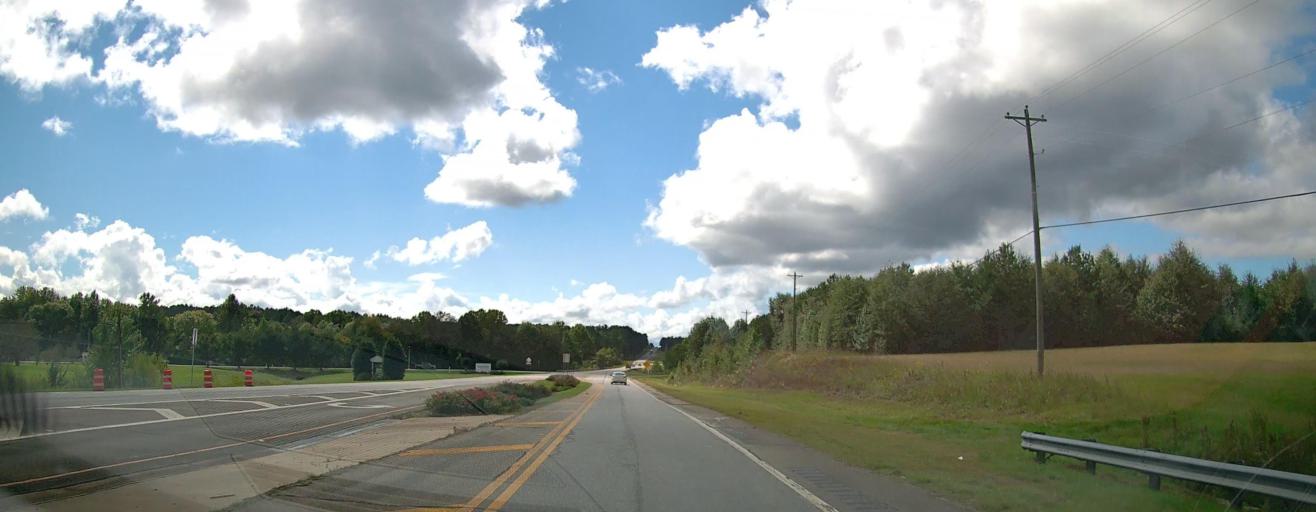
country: US
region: Georgia
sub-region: Baldwin County
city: Milledgeville
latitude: 33.0876
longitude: -83.2880
